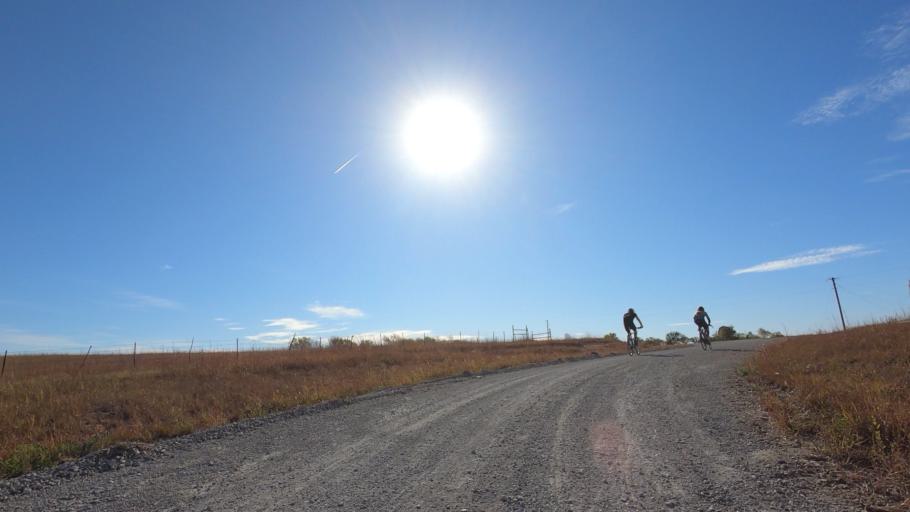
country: US
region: Kansas
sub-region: Pottawatomie County
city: Westmoreland
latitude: 39.4796
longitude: -96.5873
